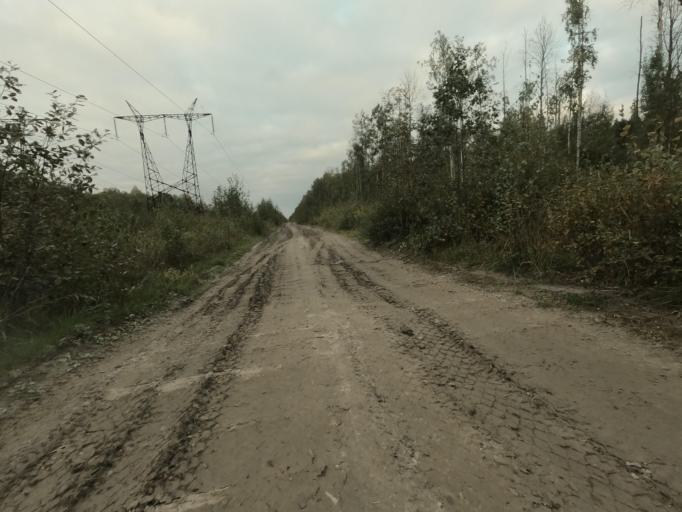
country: RU
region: St.-Petersburg
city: Sapernyy
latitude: 59.7551
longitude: 30.6892
